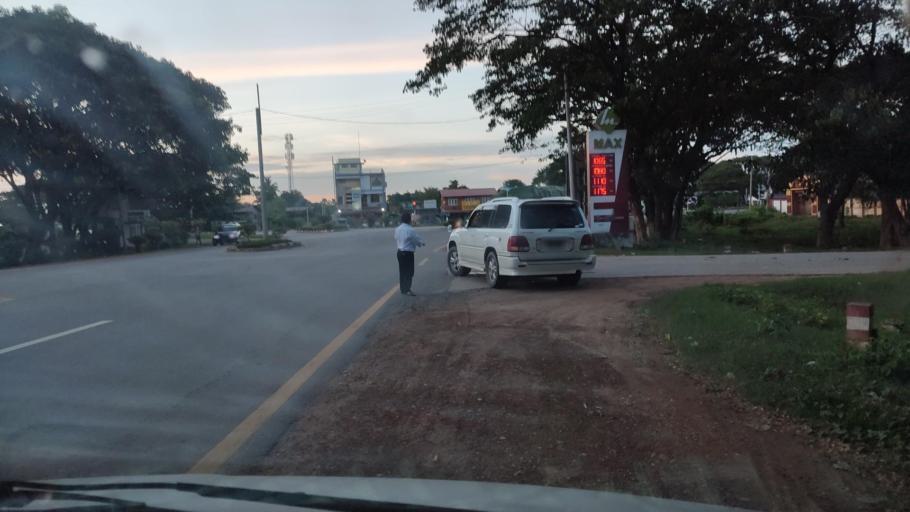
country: MM
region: Mandalay
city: Pyinmana
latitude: 19.7582
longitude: 96.2330
